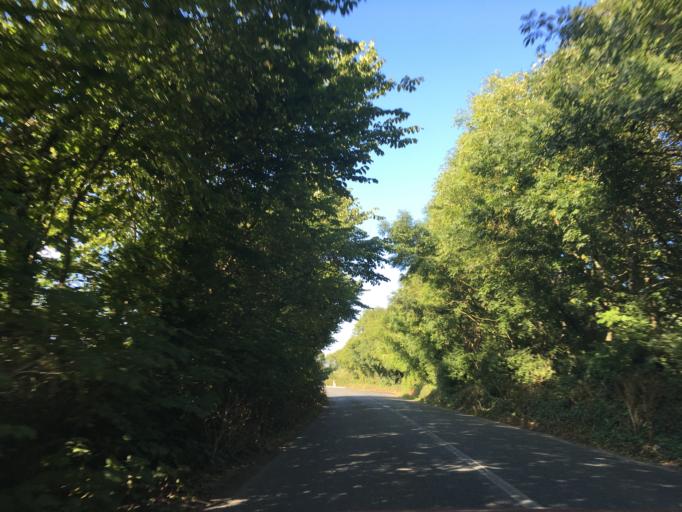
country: IE
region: Leinster
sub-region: Loch Garman
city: Loch Garman
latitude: 52.2670
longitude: -6.4779
